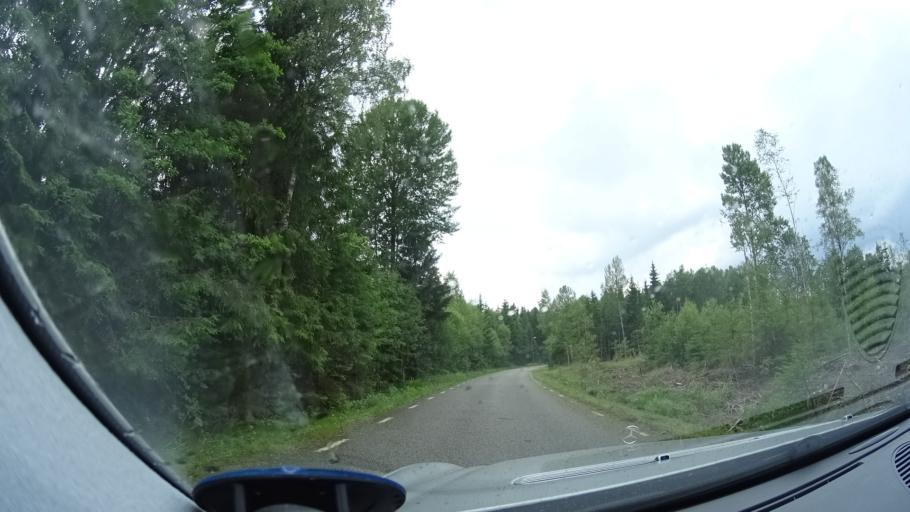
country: SE
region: Kalmar
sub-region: Emmaboda Kommun
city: Emmaboda
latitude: 56.6547
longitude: 15.7115
